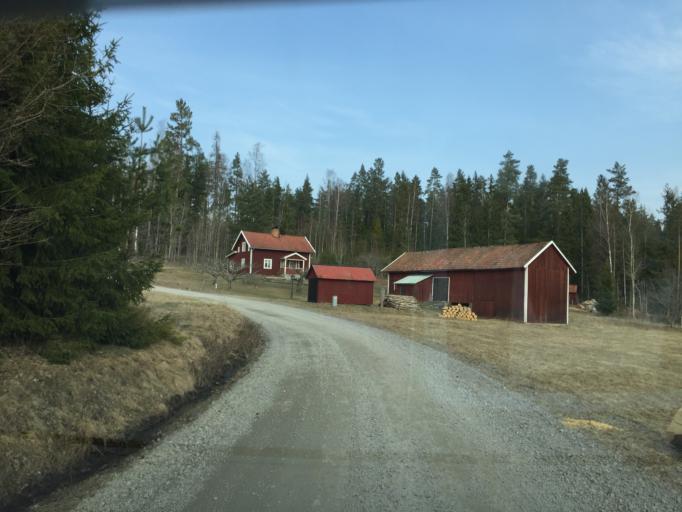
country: SE
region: Soedermanland
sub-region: Vingakers Kommun
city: Vingaker
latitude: 59.0246
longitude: 15.7777
